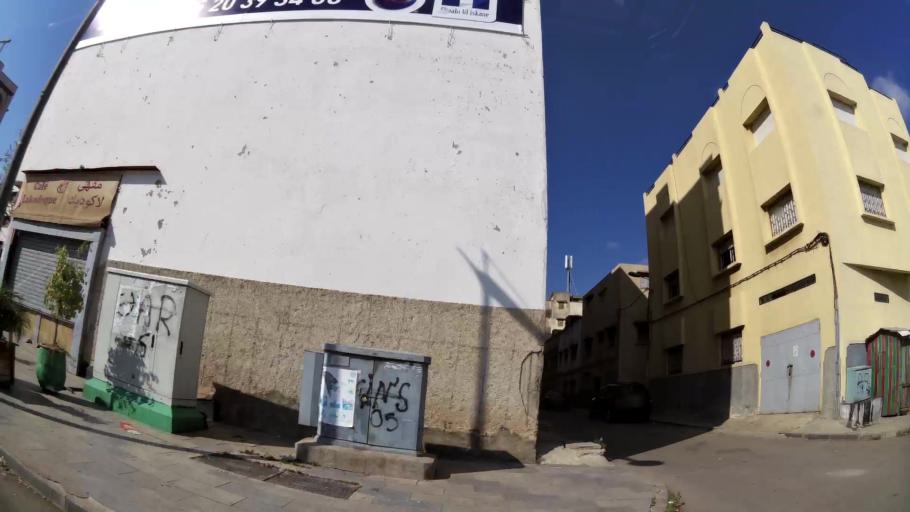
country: MA
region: Rabat-Sale-Zemmour-Zaer
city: Sale
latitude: 34.0530
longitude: -6.7954
